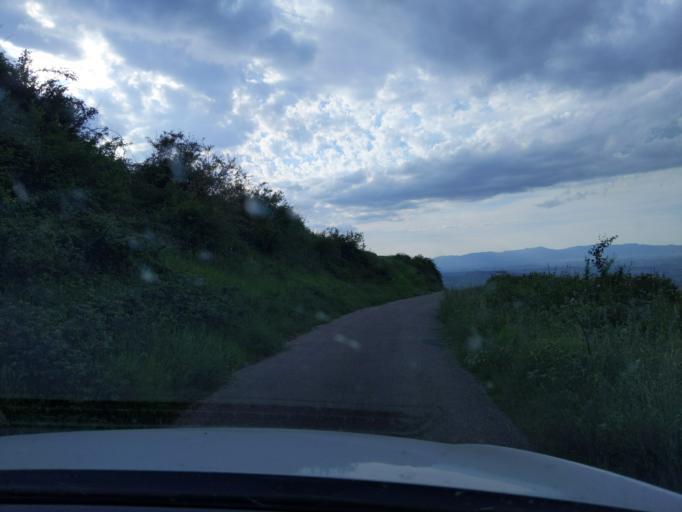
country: ES
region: La Rioja
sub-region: Provincia de La Rioja
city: Clavijo
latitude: 42.3518
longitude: -2.4318
